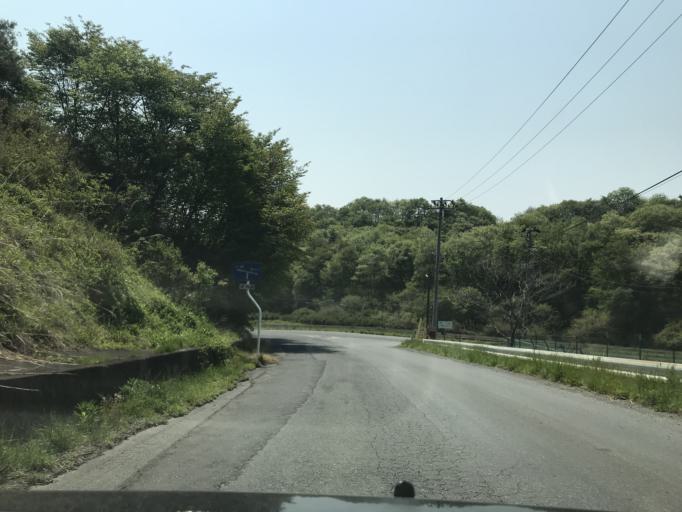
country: JP
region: Iwate
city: Ichinoseki
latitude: 38.8489
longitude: 141.0560
